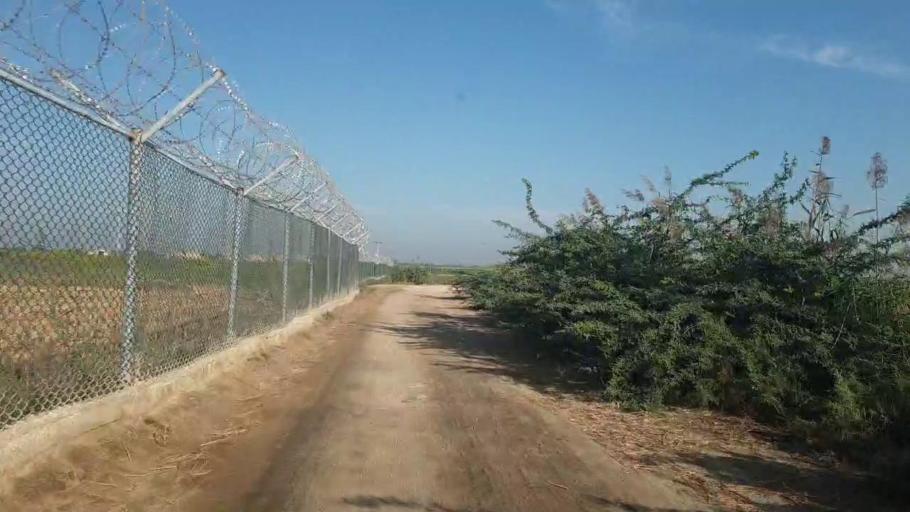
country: PK
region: Sindh
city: Talhar
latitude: 24.8444
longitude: 68.8543
